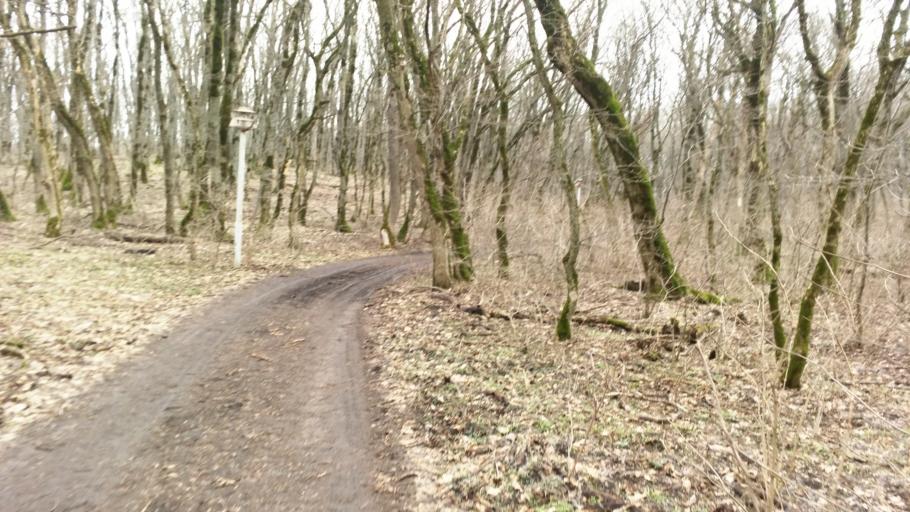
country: RU
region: Stavropol'skiy
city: Zheleznovodsk
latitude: 44.1593
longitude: 43.0403
